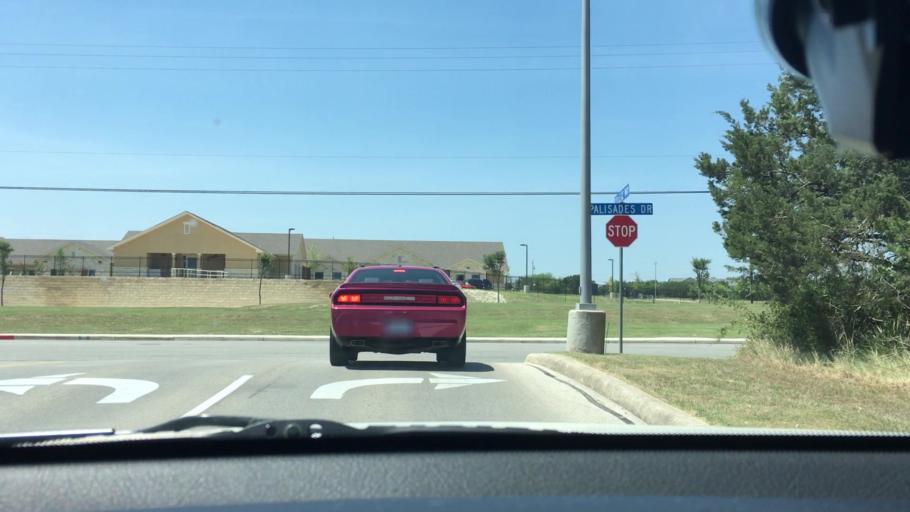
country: US
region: Texas
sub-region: Bexar County
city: Live Oak
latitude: 29.5523
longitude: -98.3259
